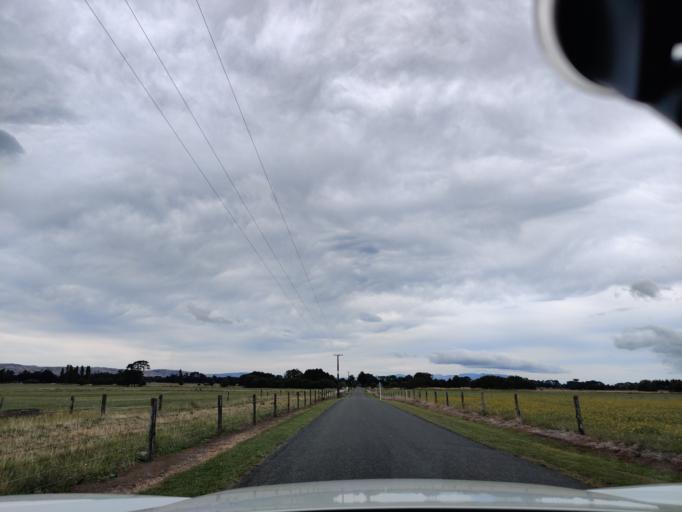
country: NZ
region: Wellington
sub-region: Masterton District
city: Masterton
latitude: -41.0298
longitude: 175.4462
